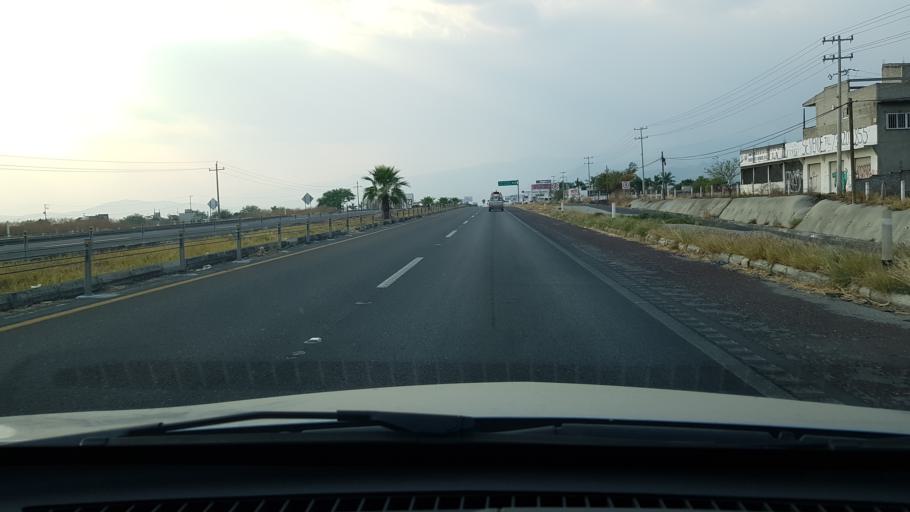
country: MX
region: Morelos
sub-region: Cuautla
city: Tierra Larga (Campo Nuevo)
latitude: 18.8608
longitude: -98.9458
